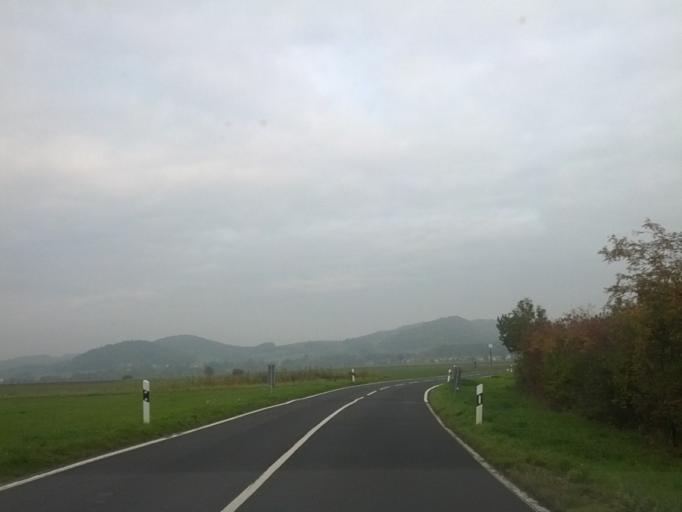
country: DE
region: Hesse
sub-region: Regierungsbezirk Kassel
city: Herleshausen
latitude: 51.0021
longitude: 10.1869
